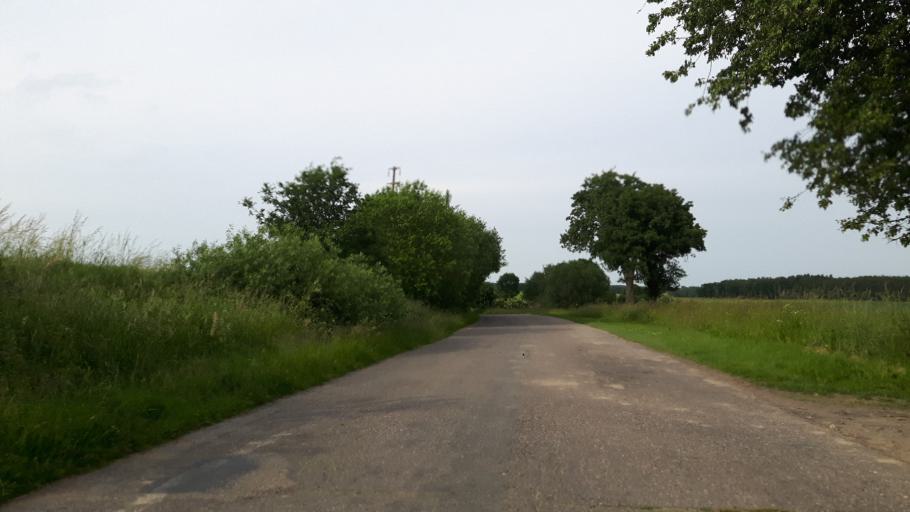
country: PL
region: West Pomeranian Voivodeship
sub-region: Powiat gryficki
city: Gryfice
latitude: 53.8707
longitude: 15.1792
